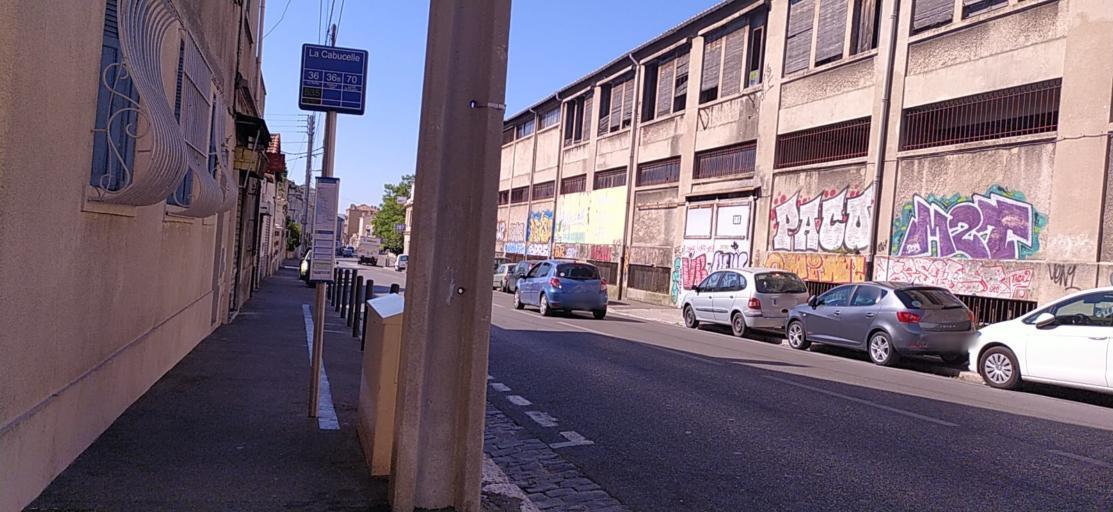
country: FR
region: Provence-Alpes-Cote d'Azur
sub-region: Departement des Bouches-du-Rhone
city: Marseille 14
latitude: 43.3360
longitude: 5.3576
